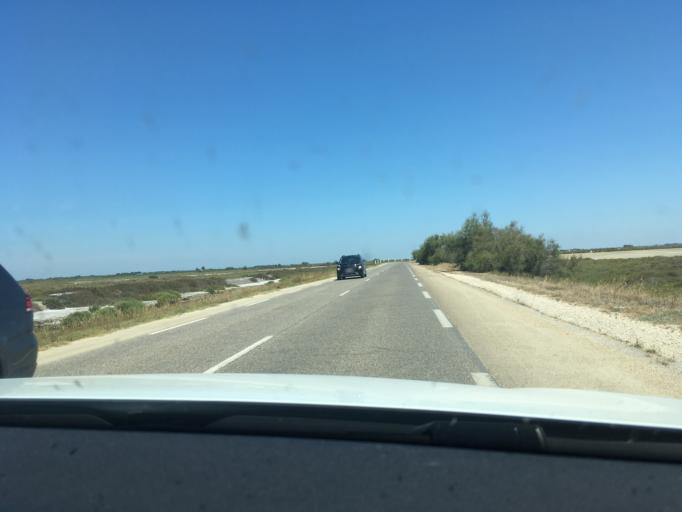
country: FR
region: Provence-Alpes-Cote d'Azur
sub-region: Departement des Bouches-du-Rhone
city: Saintes-Maries-de-la-Mer
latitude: 43.4726
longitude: 4.4363
